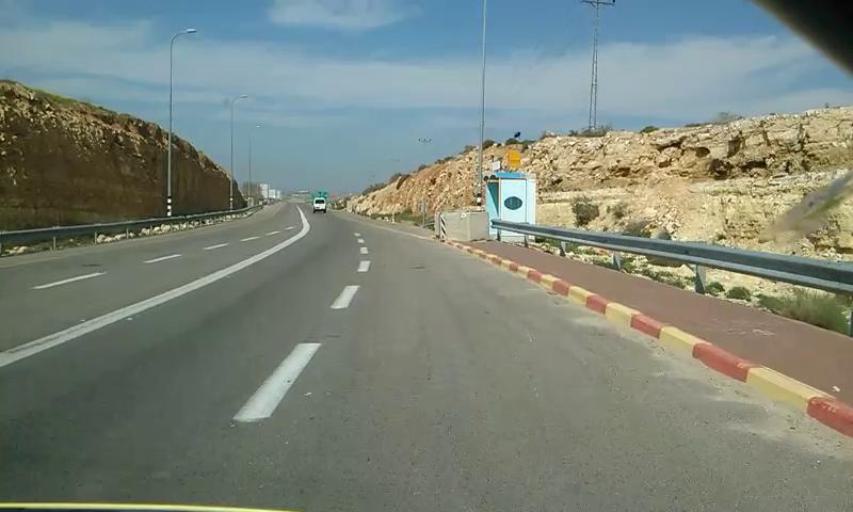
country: PS
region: West Bank
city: Az Zahiriyah
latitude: 31.3785
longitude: 35.0042
